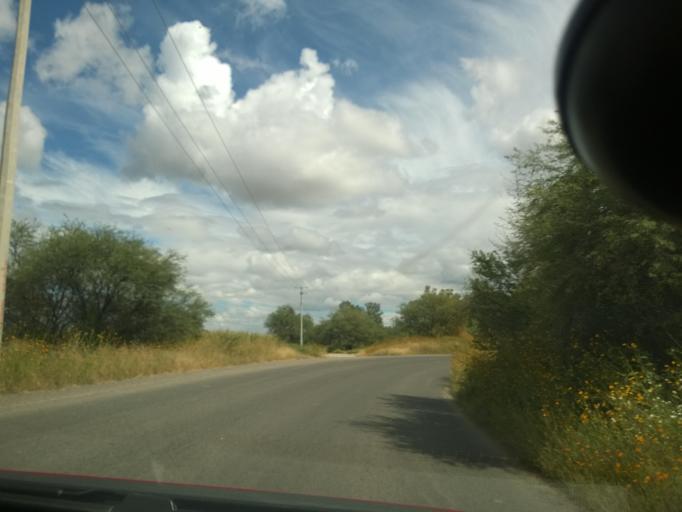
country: MX
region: Guanajuato
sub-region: Leon
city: El CERESO
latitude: 20.9910
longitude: -101.6530
